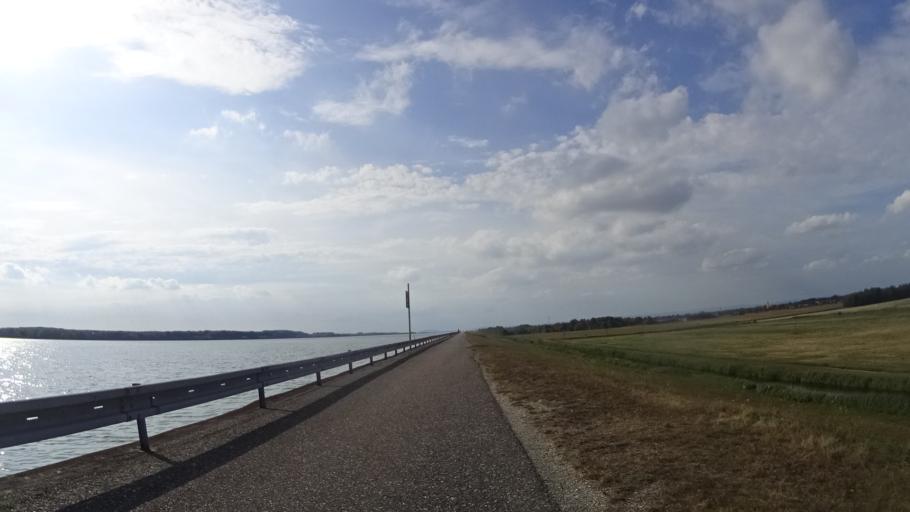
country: HU
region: Gyor-Moson-Sopron
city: Asvanyraro
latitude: 47.9307
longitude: 17.4701
